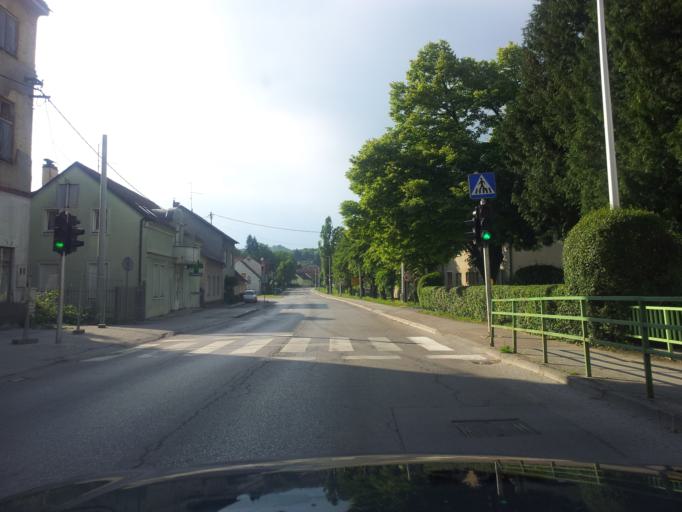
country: HR
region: Karlovacka
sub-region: Grad Karlovac
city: Karlovac
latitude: 45.4529
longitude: 15.4952
